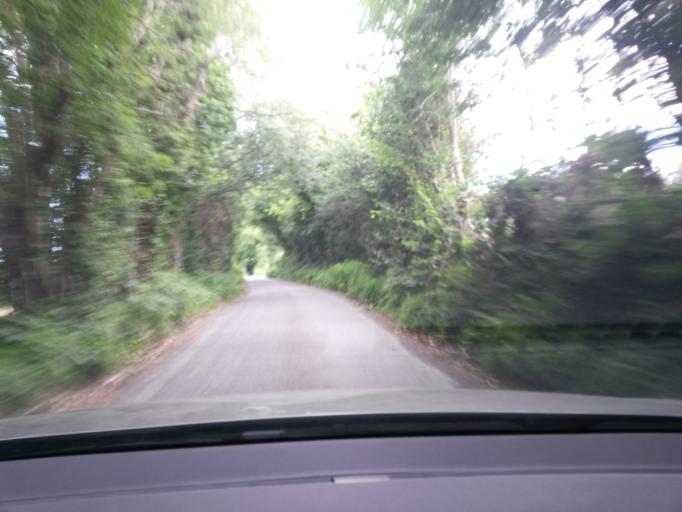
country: IE
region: Leinster
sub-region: Wicklow
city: Enniskerry
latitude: 53.1641
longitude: -6.2133
